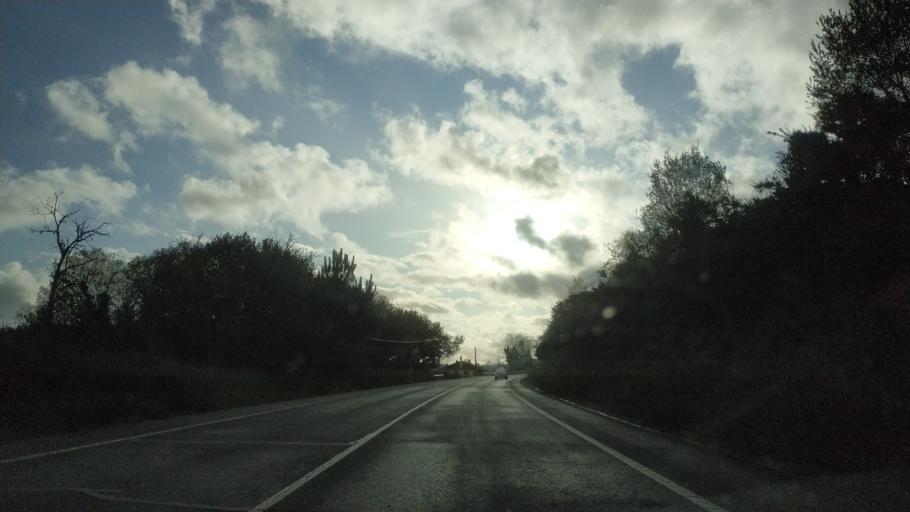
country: ES
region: Galicia
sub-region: Provincia da Coruna
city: Arzua
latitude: 42.8926
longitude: -8.1714
